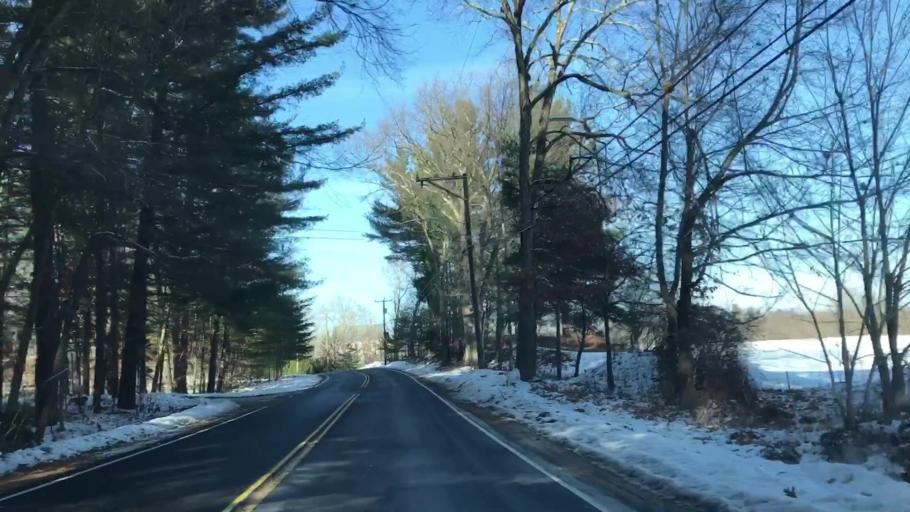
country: US
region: New Hampshire
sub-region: Hillsborough County
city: Milford
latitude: 42.8253
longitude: -71.6070
